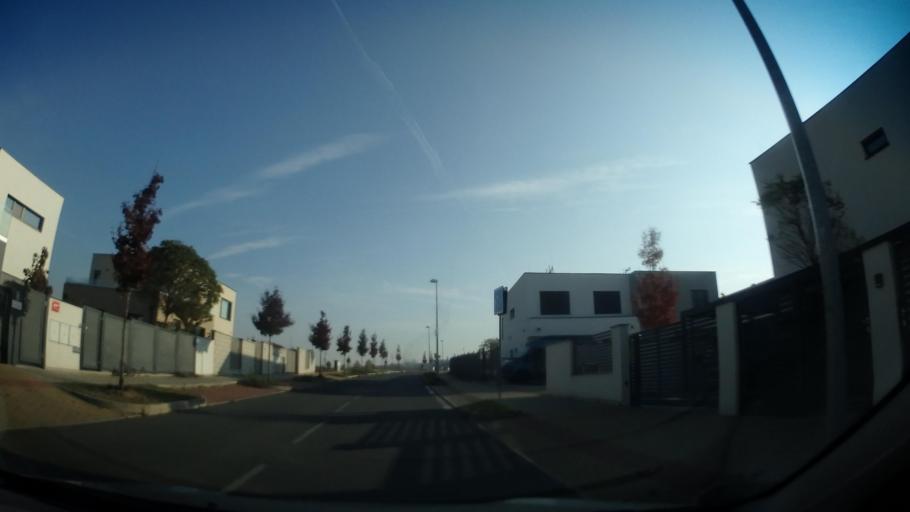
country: CZ
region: Praha
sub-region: Praha 14
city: Dolni Pocernice
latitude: 50.0921
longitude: 14.5789
